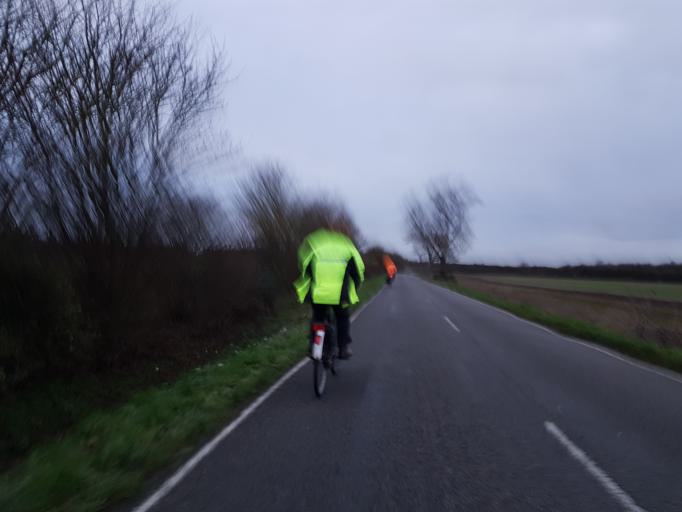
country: GB
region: England
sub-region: Cambridgeshire
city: Fulbourn
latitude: 52.2147
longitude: 0.1959
